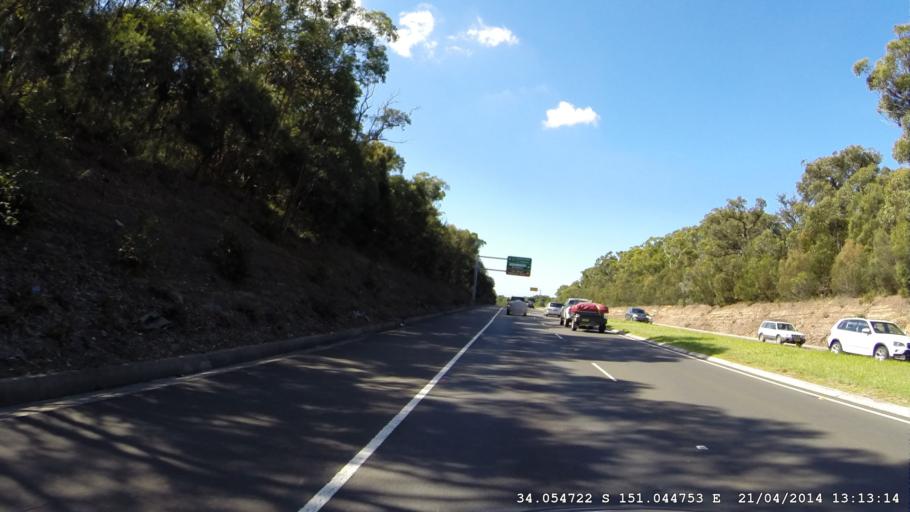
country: AU
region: New South Wales
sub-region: Sutherland Shire
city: Loftus
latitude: -34.0547
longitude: 151.0448
